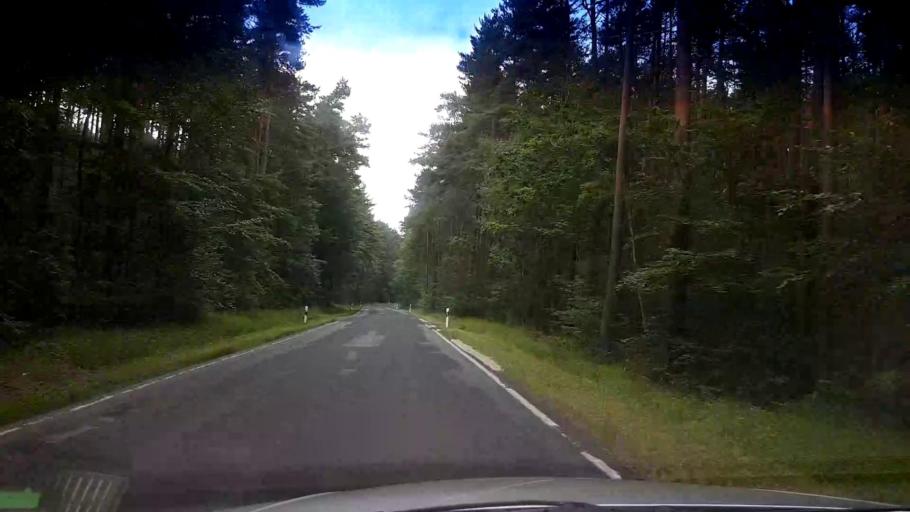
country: DE
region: Bavaria
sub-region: Upper Franconia
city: Oberhaid
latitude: 49.9508
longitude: 10.8132
